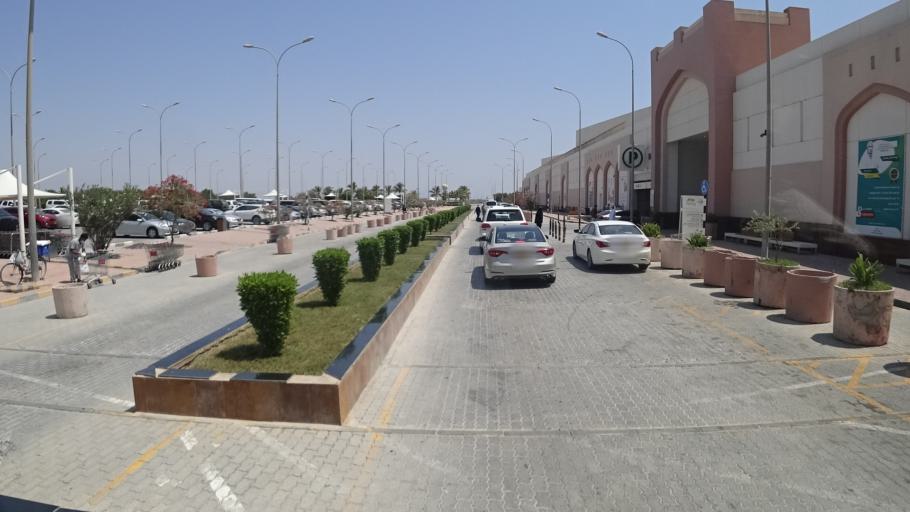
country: OM
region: Zufar
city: Salalah
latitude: 17.0244
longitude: 54.0658
